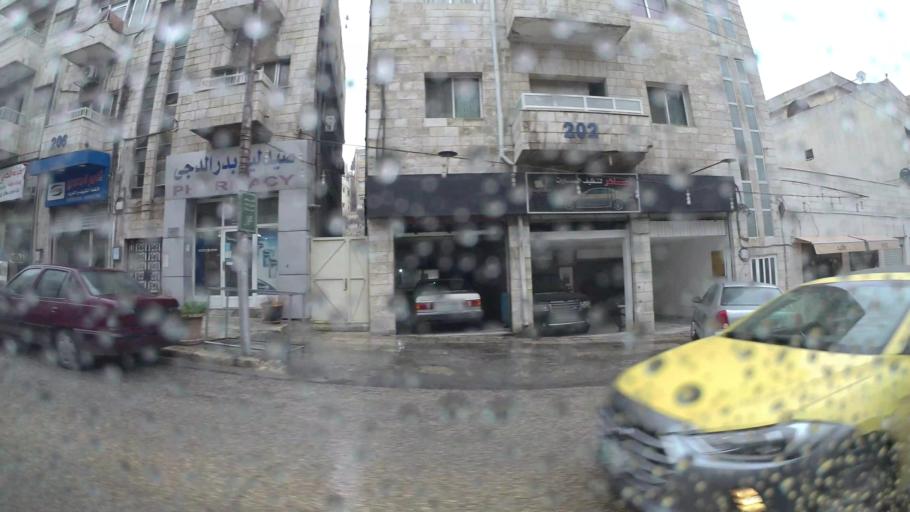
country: JO
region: Amman
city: Amman
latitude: 31.9536
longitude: 35.9201
